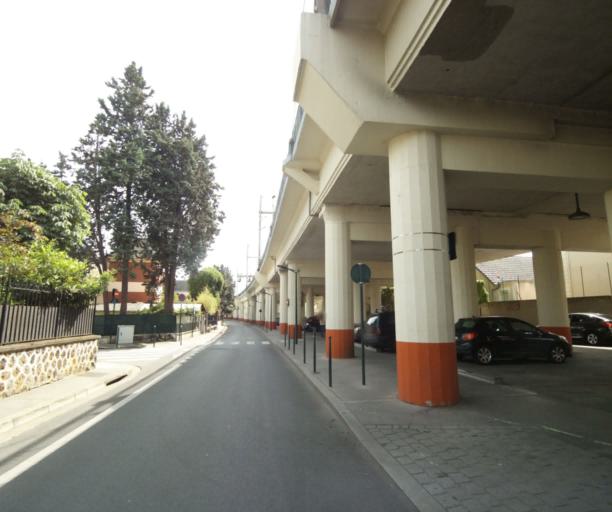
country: FR
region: Ile-de-France
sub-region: Departement des Hauts-de-Seine
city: Colombes
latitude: 48.9282
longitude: 2.2595
